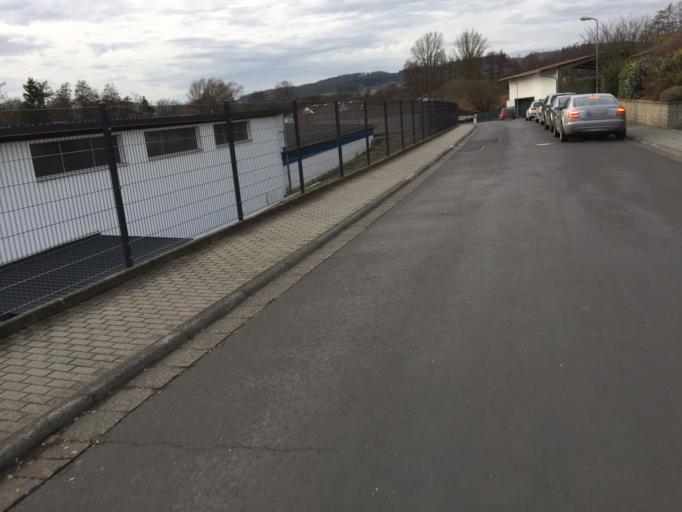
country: DE
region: Hesse
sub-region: Regierungsbezirk Giessen
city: Rabenau
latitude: 50.6782
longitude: 8.8521
